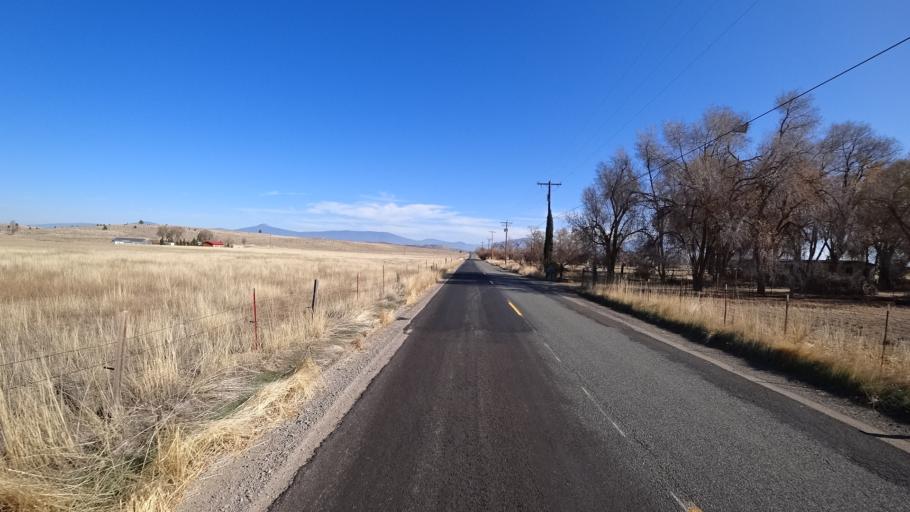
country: US
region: California
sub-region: Siskiyou County
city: Montague
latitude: 41.5746
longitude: -122.5391
